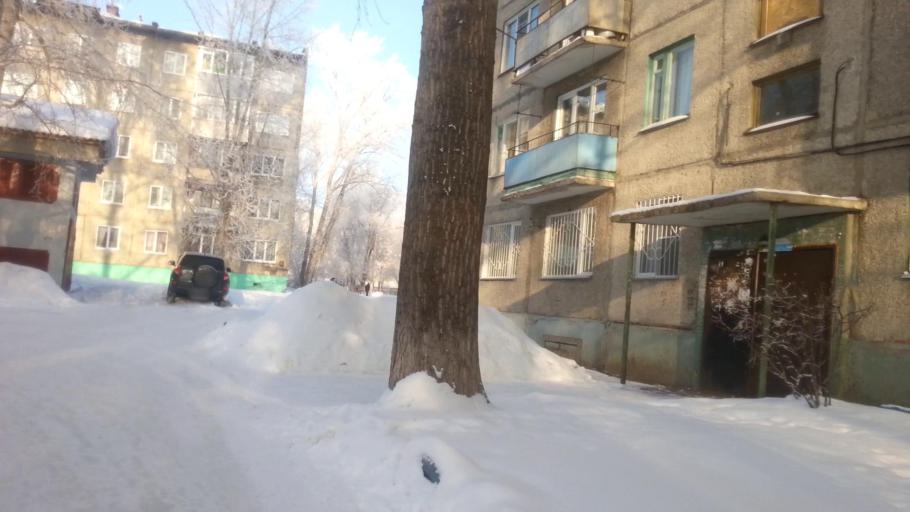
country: RU
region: Altai Krai
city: Novosilikatnyy
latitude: 53.3773
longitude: 83.6728
